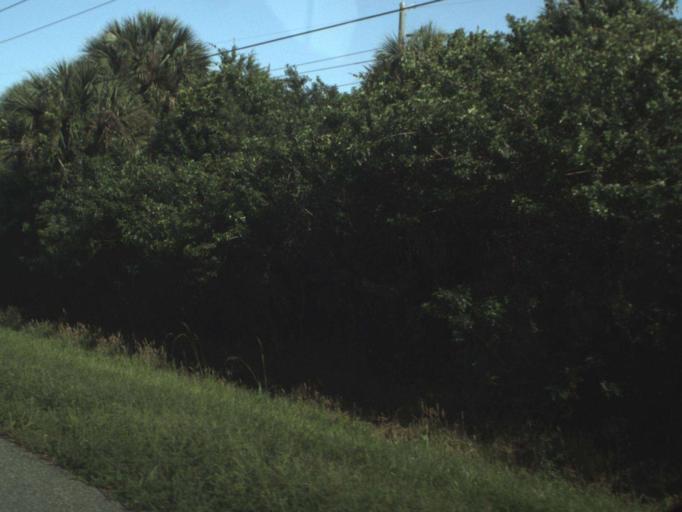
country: US
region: Florida
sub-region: Seminole County
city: Geneva
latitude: 28.7161
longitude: -81.0517
